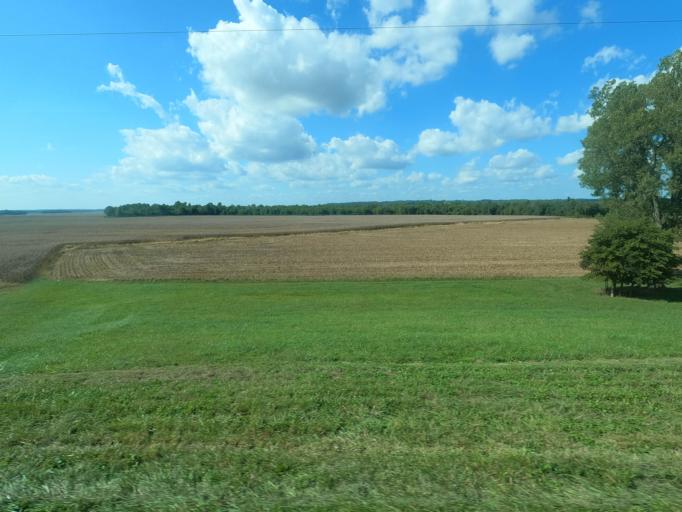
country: US
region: Illinois
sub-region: Massac County
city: Metropolis
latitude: 37.2687
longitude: -88.7599
